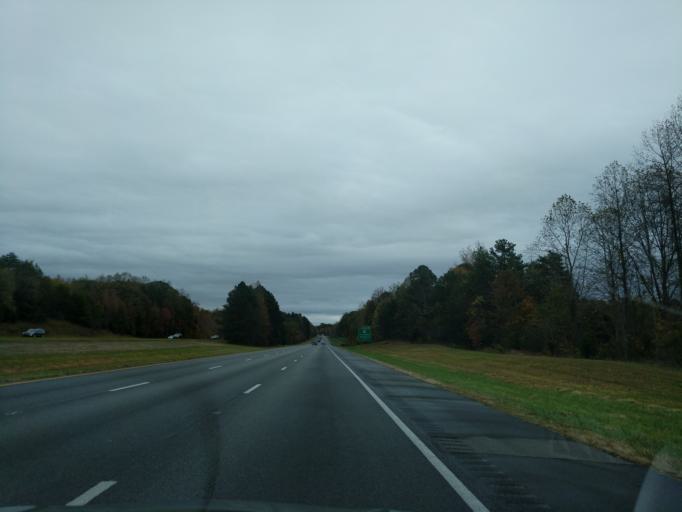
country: US
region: North Carolina
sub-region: Davidson County
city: Lexington
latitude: 35.8001
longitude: -80.2029
